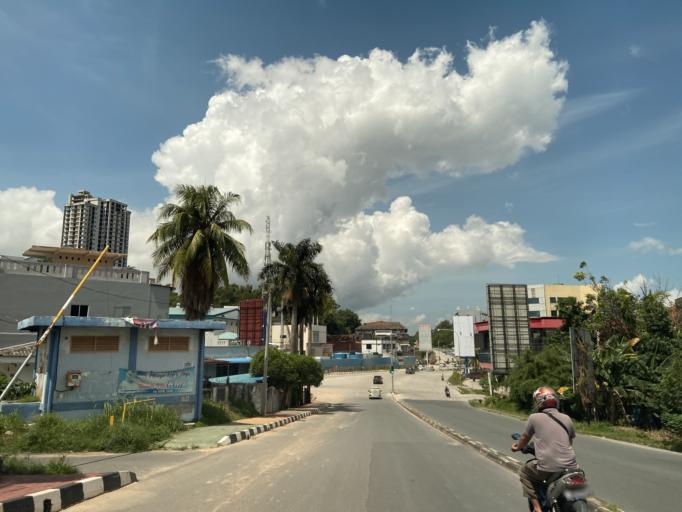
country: SG
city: Singapore
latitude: 1.1417
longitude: 104.0156
